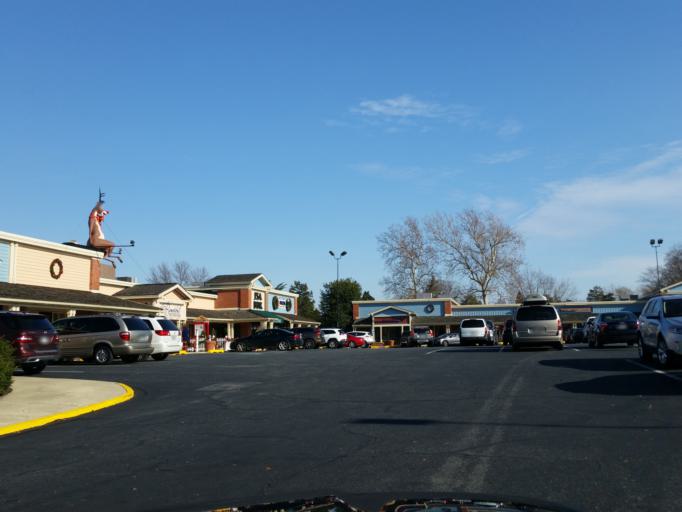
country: US
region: Maryland
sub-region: Talbot County
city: Easton
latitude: 38.7781
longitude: -76.0759
